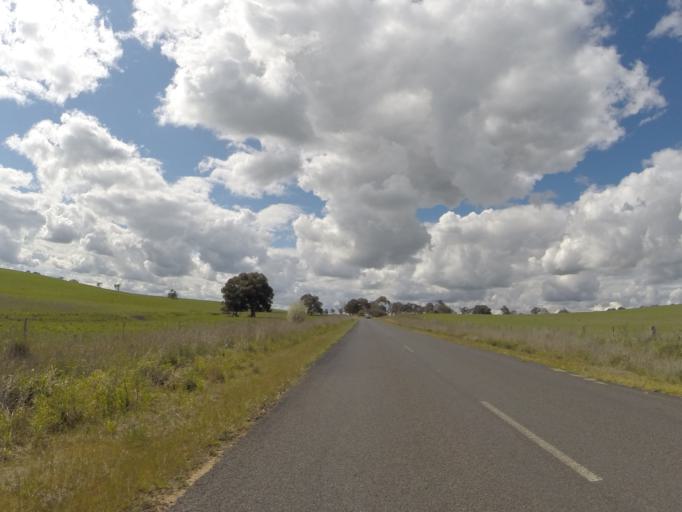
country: AU
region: New South Wales
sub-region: Yass Valley
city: Yass
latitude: -34.9156
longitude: 148.8824
